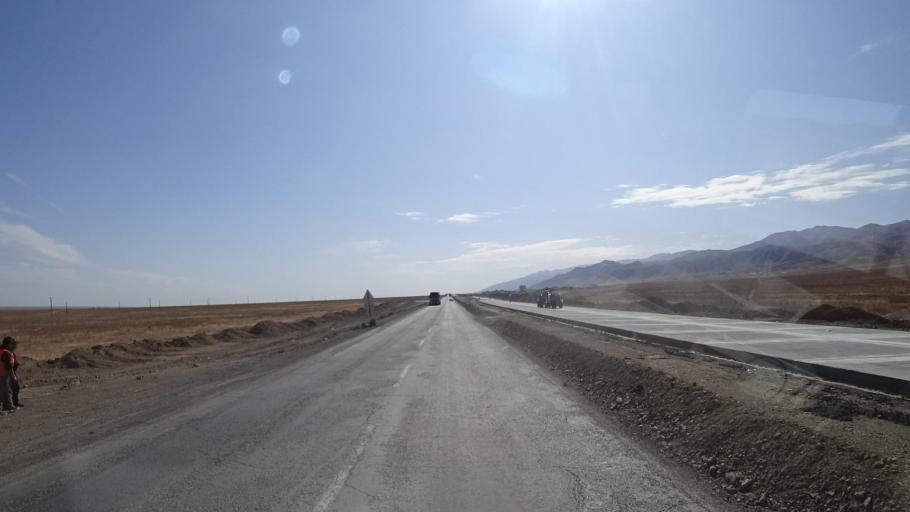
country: KG
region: Chuy
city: Ivanovka
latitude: 43.3965
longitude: 75.1250
